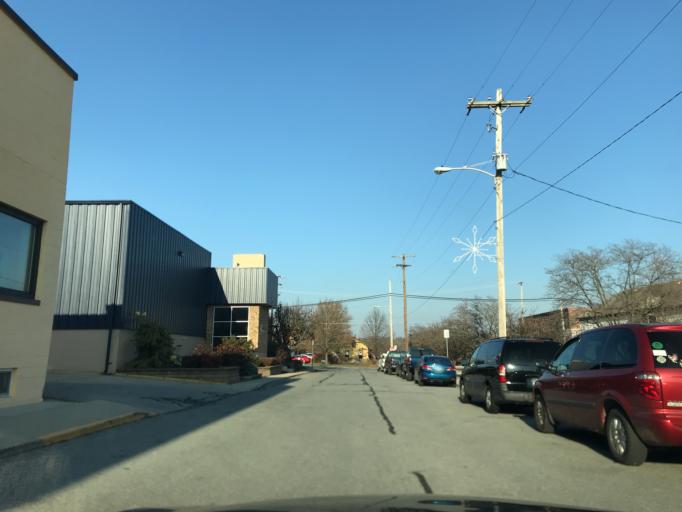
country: US
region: Pennsylvania
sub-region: York County
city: New Freedom
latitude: 39.7388
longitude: -76.7015
